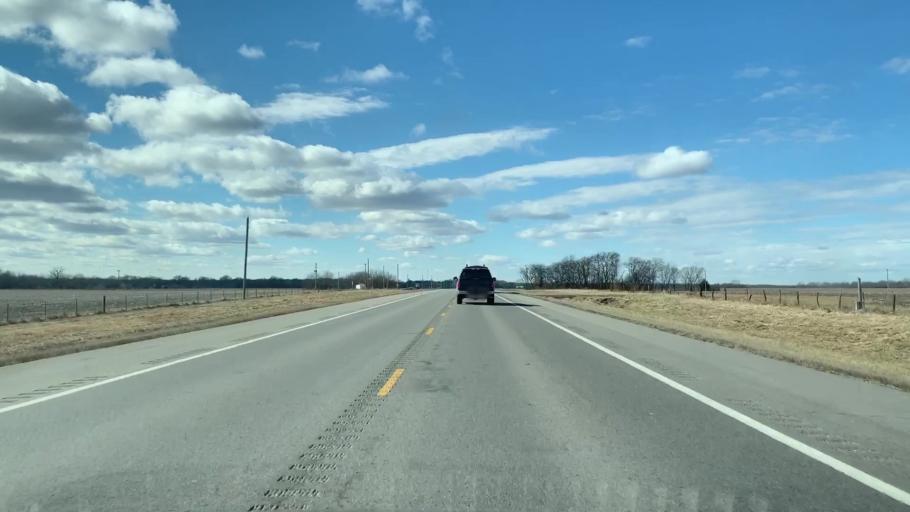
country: US
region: Kansas
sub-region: Cherokee County
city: Columbus
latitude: 37.3397
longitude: -94.8654
